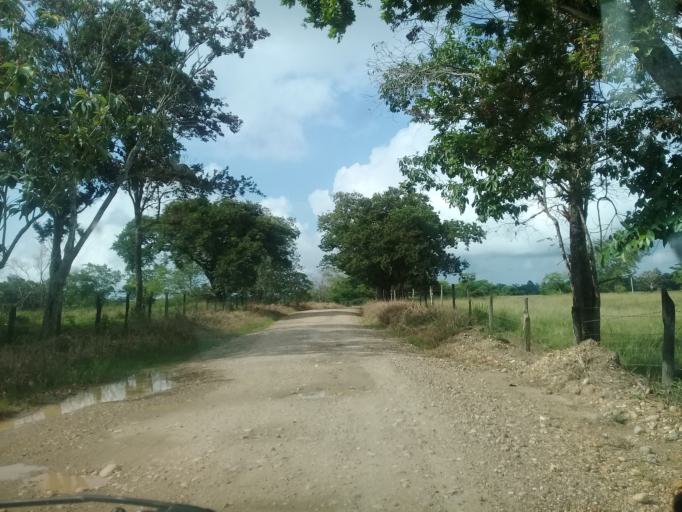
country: CO
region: Antioquia
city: Puerto Triunfo
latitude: 5.7020
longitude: -74.6009
